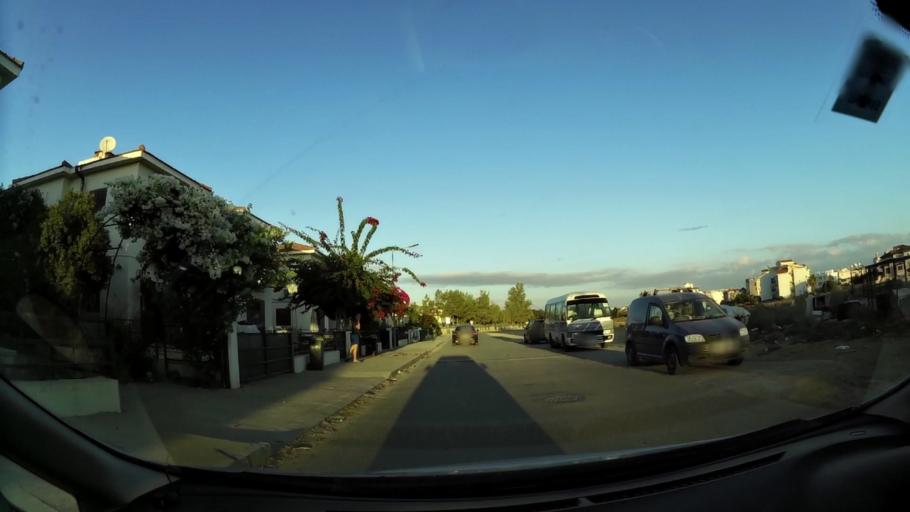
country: CY
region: Lefkosia
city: Nicosia
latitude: 35.2026
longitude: 33.3271
